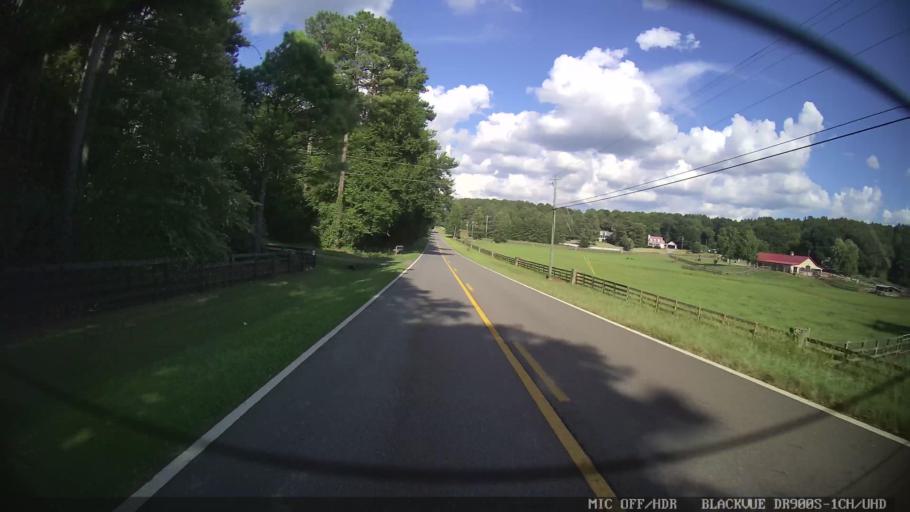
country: US
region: Georgia
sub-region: Bartow County
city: Euharlee
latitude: 34.1739
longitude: -84.9839
